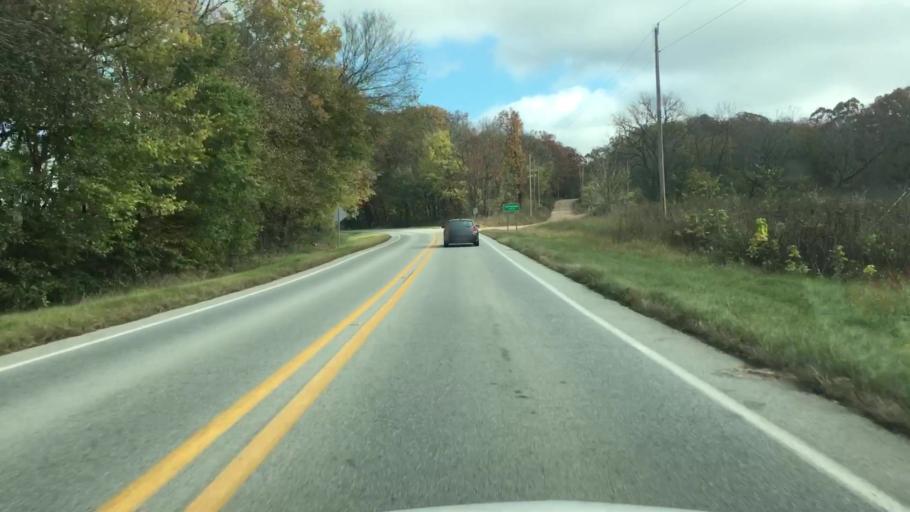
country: US
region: Arkansas
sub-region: Benton County
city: Gentry
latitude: 36.2559
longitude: -94.4326
